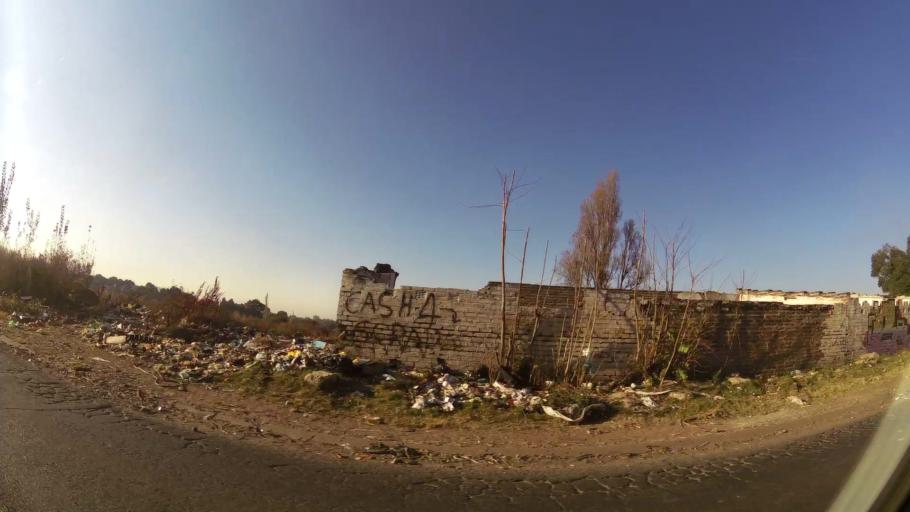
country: ZA
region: Gauteng
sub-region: Ekurhuleni Metropolitan Municipality
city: Germiston
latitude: -26.1967
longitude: 28.1524
